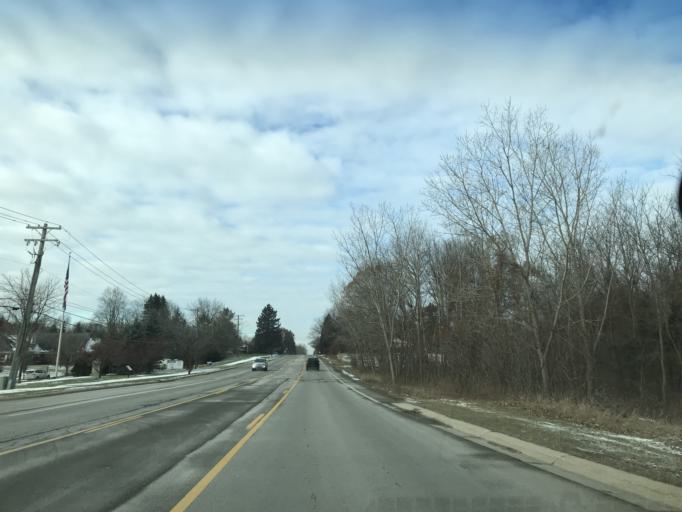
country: US
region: Michigan
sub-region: Oakland County
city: Clarkston
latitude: 42.7338
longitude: -83.3825
